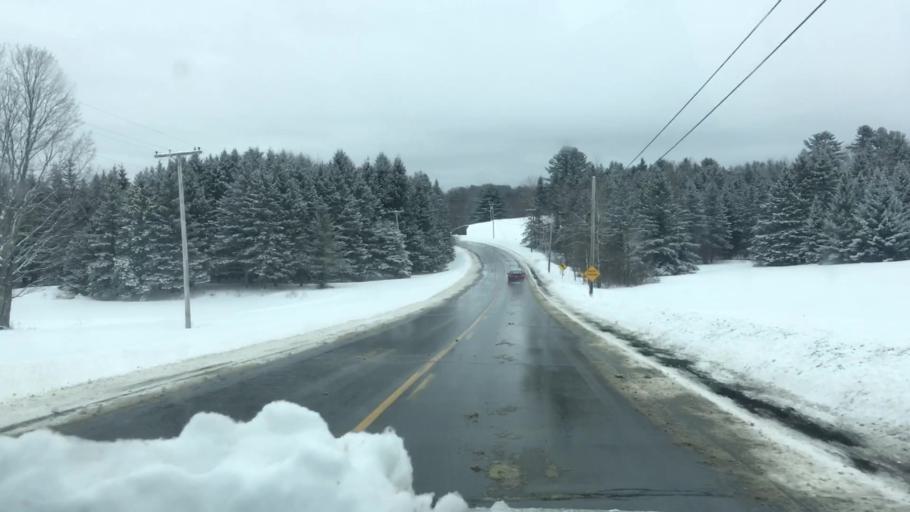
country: US
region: Maine
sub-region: Penobscot County
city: Charleston
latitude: 44.9960
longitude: -69.0420
